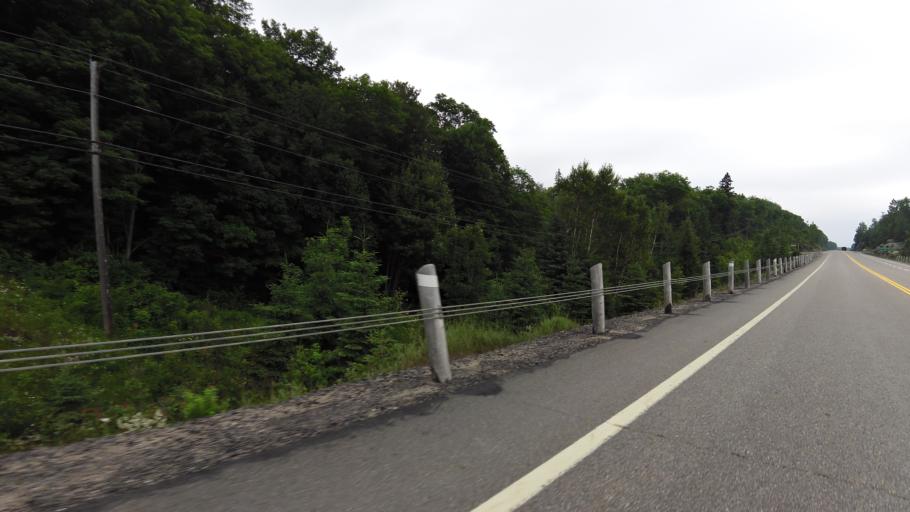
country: CA
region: Ontario
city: Huntsville
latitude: 45.3413
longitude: -78.9444
